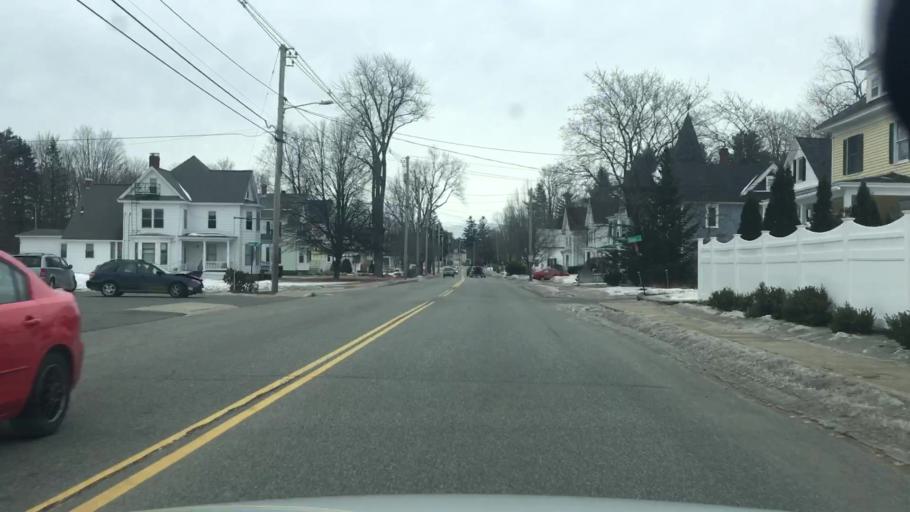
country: US
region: Maine
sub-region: York County
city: Springvale
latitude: 43.4628
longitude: -70.7953
